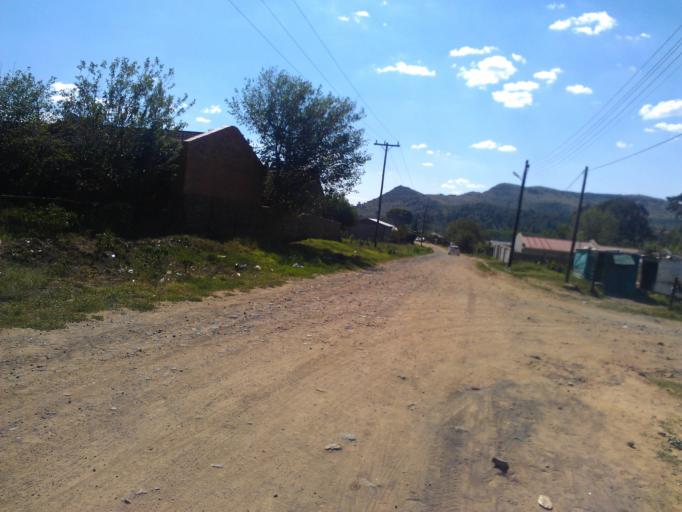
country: LS
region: Maseru
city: Maseru
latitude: -29.3016
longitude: 27.4644
